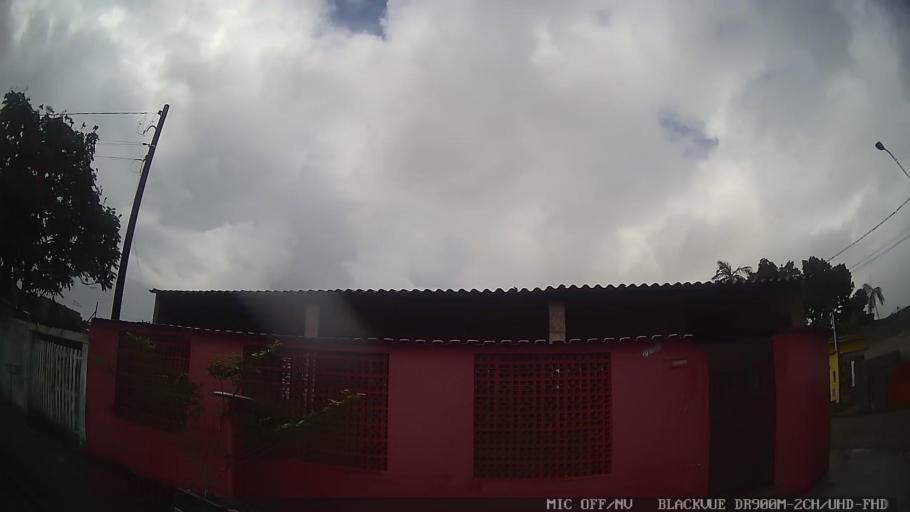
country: BR
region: Sao Paulo
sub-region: Itanhaem
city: Itanhaem
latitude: -24.1894
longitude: -46.8221
